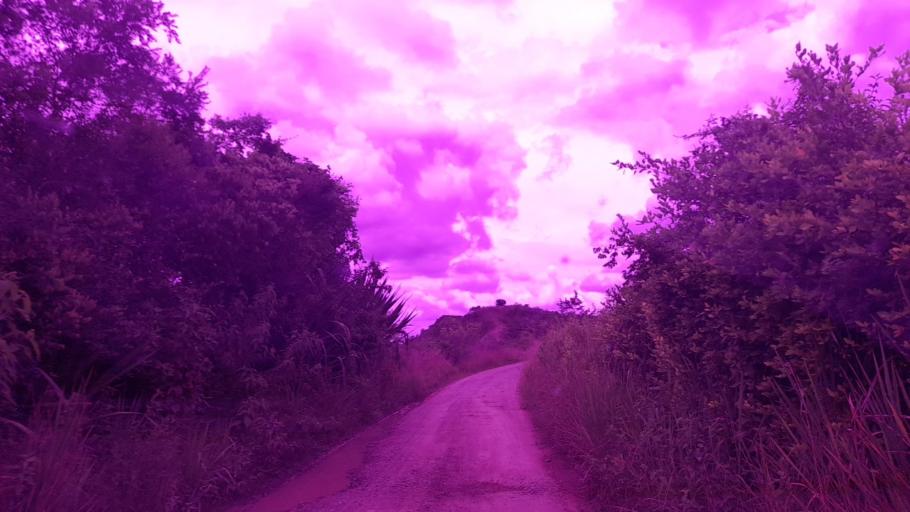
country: CO
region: Valle del Cauca
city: Andalucia
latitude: 4.1748
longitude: -76.1161
